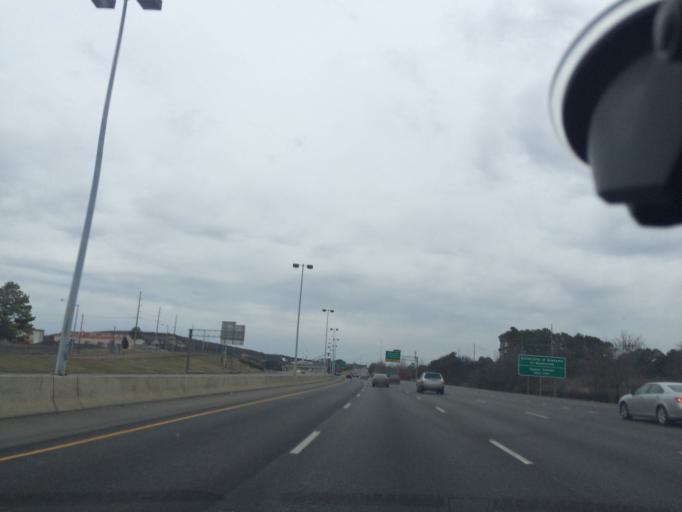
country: US
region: Alabama
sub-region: Madison County
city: Redstone Arsenal
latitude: 34.7184
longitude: -86.6342
